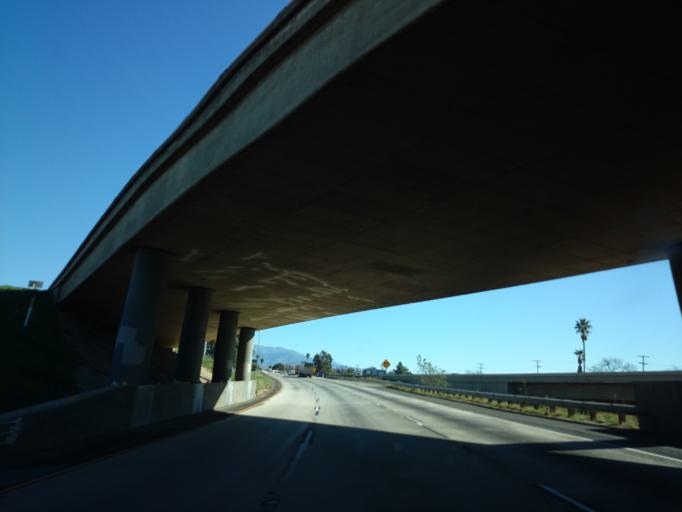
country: US
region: California
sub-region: Riverside County
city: Beaumont
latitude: 33.9333
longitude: -116.9908
